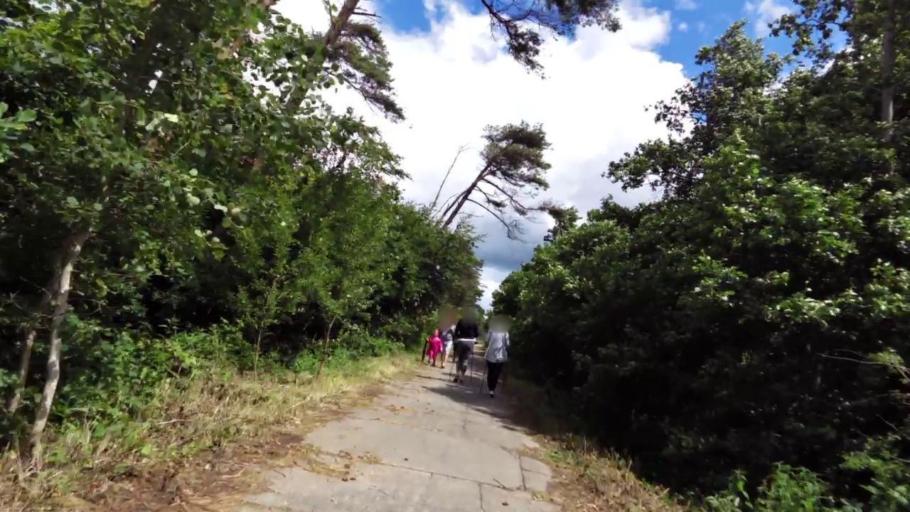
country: PL
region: West Pomeranian Voivodeship
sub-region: Powiat slawienski
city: Darlowo
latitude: 54.4950
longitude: 16.4461
